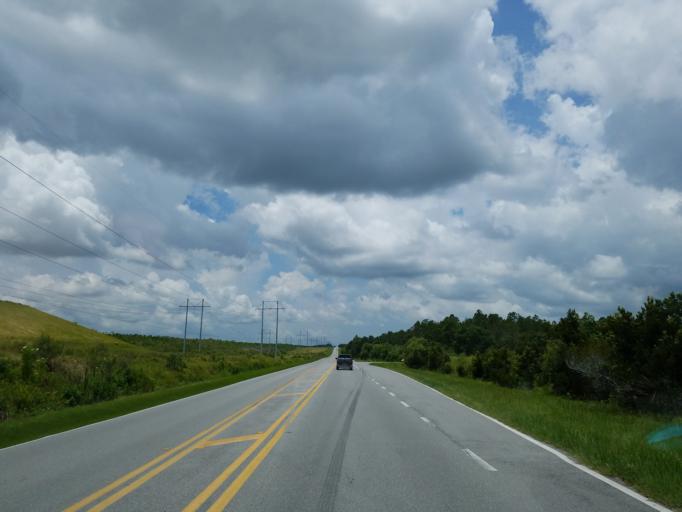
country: US
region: Florida
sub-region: Polk County
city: Fuller Heights
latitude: 27.8508
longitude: -82.0161
